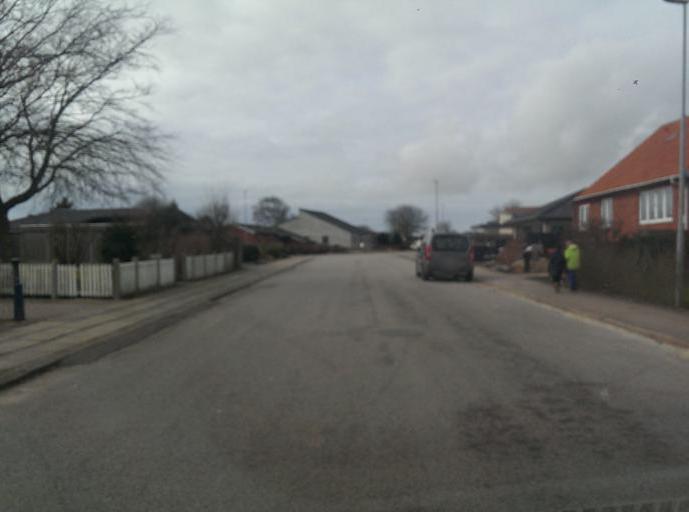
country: DK
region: South Denmark
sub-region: Esbjerg Kommune
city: Esbjerg
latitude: 55.4982
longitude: 8.4155
